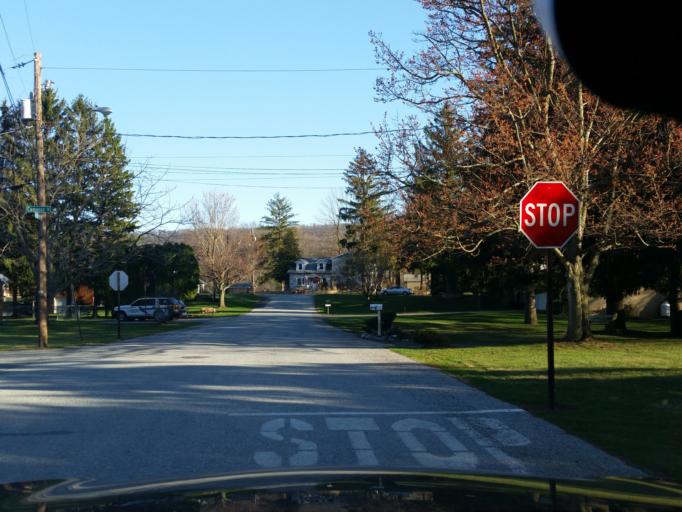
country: US
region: Pennsylvania
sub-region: Perry County
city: Marysville
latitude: 40.3402
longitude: -76.9382
